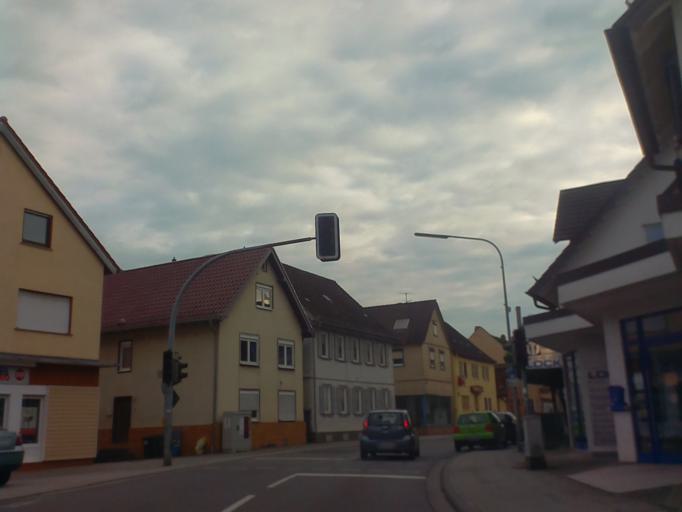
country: DE
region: Hesse
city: Hochst im Odenwald
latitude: 49.7976
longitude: 8.9935
